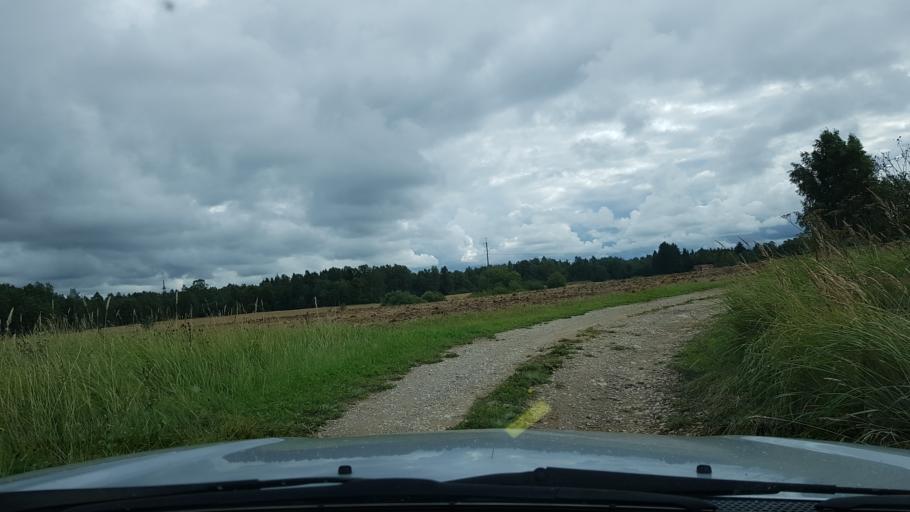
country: EE
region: Harju
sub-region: Rae vald
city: Vaida
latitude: 59.3490
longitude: 24.9869
